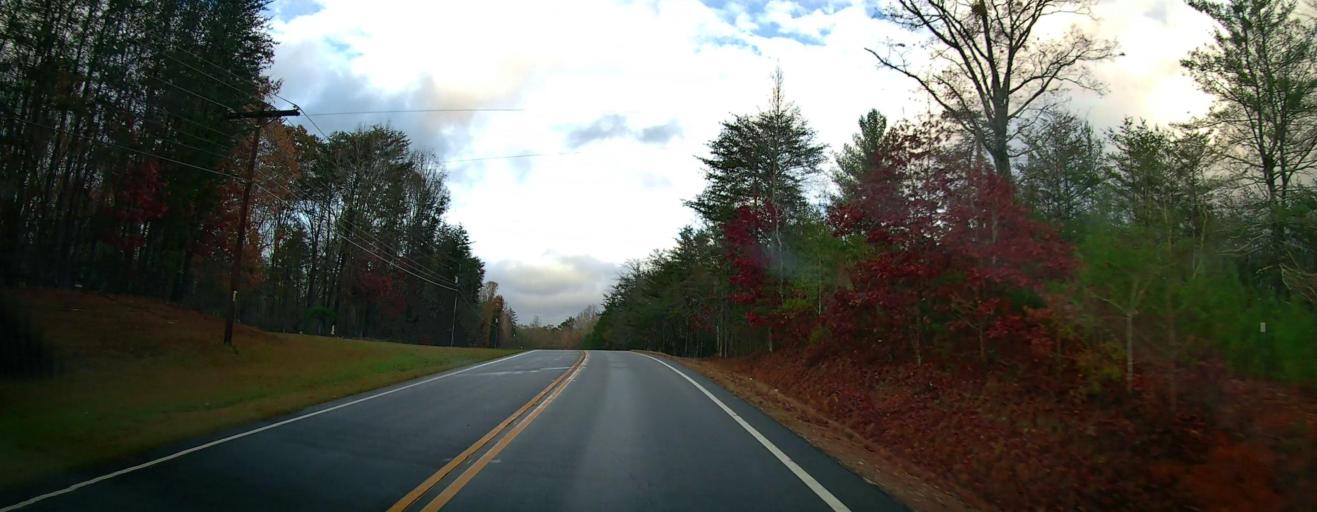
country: US
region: Georgia
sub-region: White County
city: Cleveland
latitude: 34.6319
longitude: -83.7986
